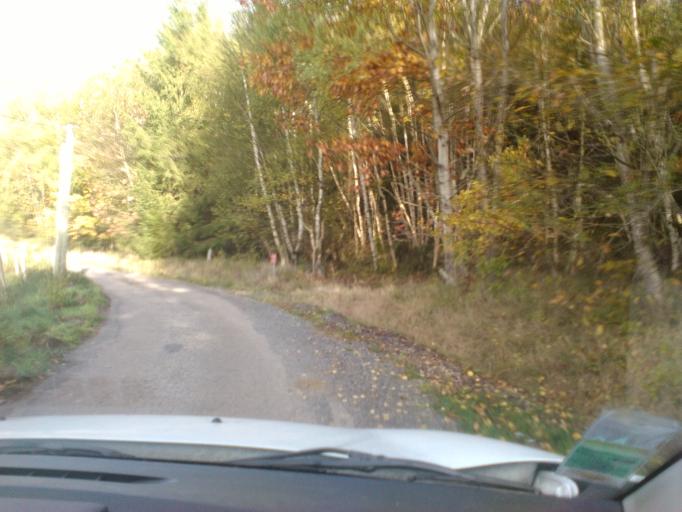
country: FR
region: Lorraine
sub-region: Departement des Vosges
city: Moyenmoutier
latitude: 48.4193
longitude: 6.8756
